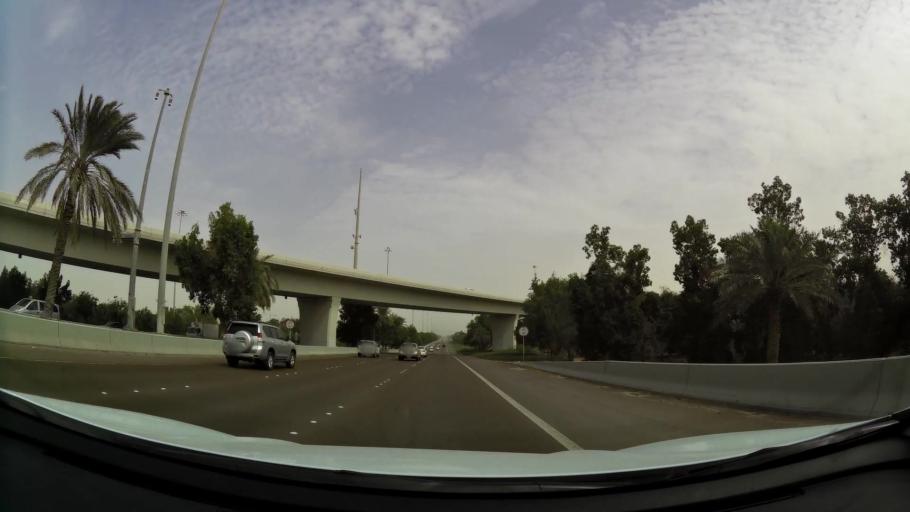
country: AE
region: Abu Dhabi
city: Abu Dhabi
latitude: 24.3908
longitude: 54.5408
